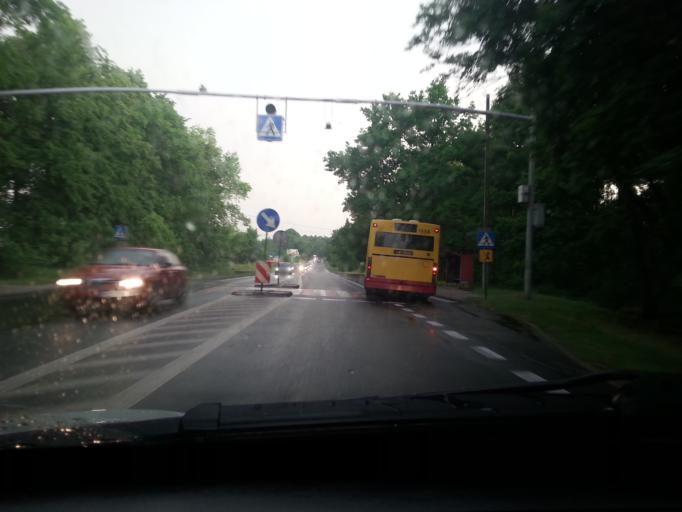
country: PL
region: Lodz Voivodeship
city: Lodz
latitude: 51.8127
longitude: 19.5031
